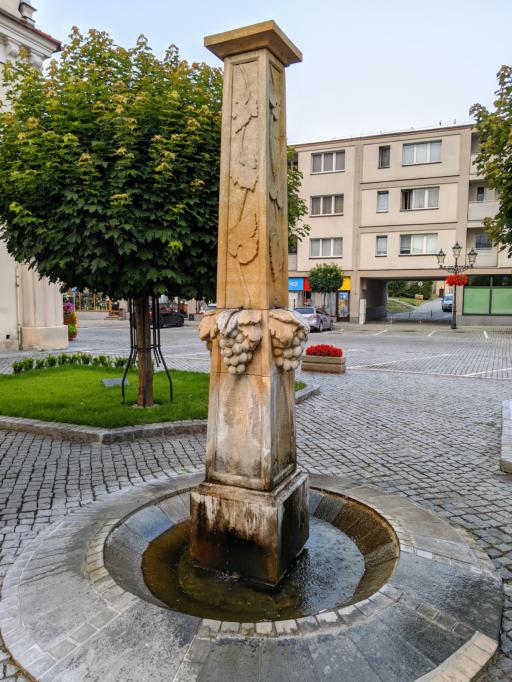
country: PL
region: Opole Voivodeship
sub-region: Powiat prudnicki
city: Glogowek
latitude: 50.3534
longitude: 17.8608
